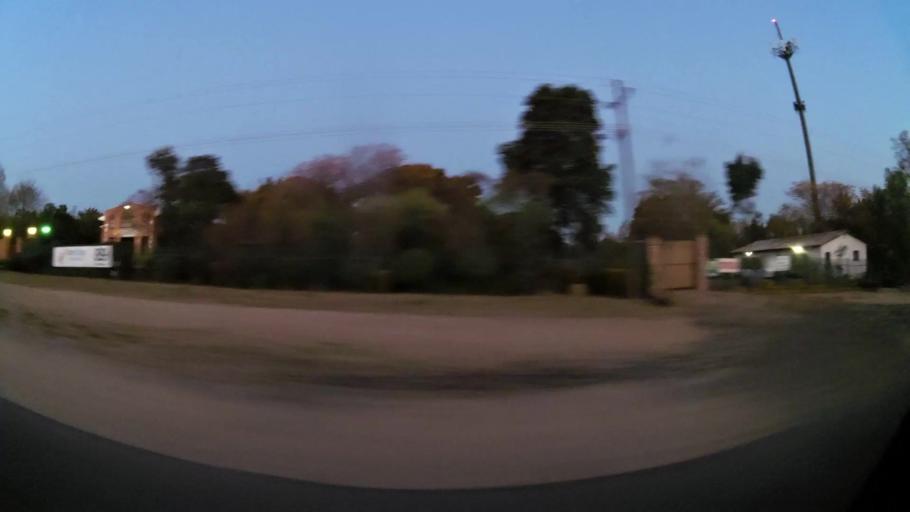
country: ZA
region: Gauteng
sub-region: City of Johannesburg Metropolitan Municipality
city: Midrand
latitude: -25.9541
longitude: 28.0869
